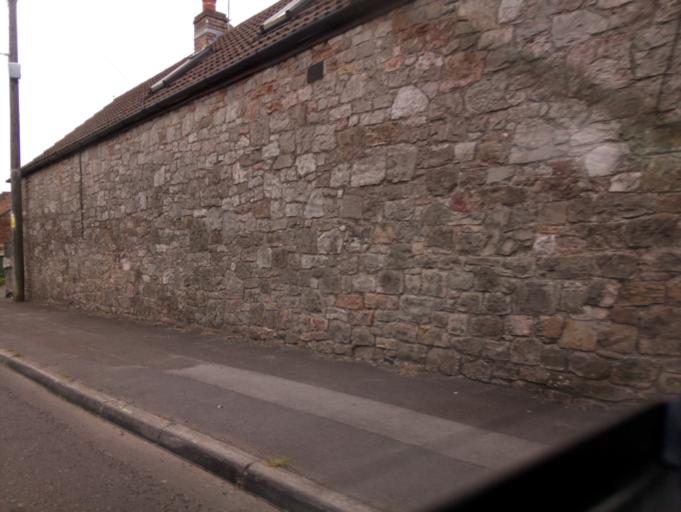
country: GB
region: England
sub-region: North Somerset
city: Congresbury
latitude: 51.3656
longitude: -2.8068
